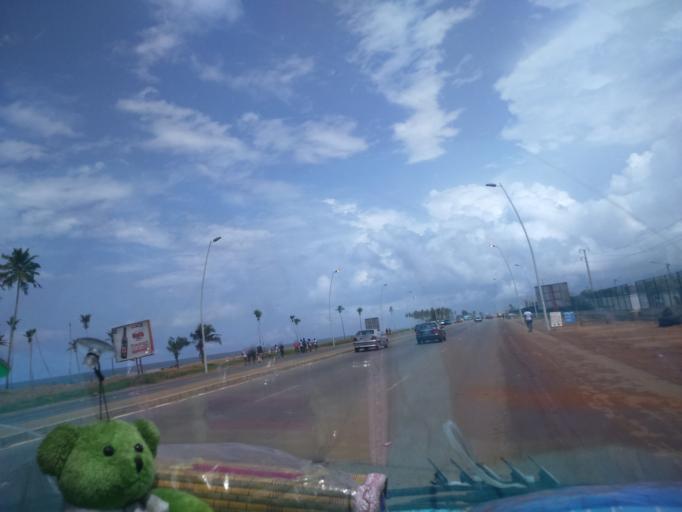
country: CI
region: Lagunes
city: Bingerville
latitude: 5.2381
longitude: -3.8876
